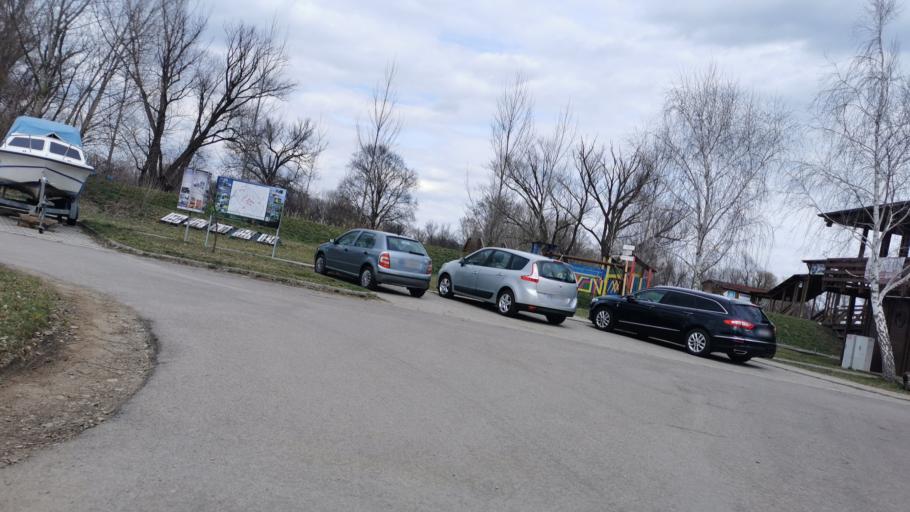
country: CZ
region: South Moravian
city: Rohatec
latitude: 48.8722
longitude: 17.2123
